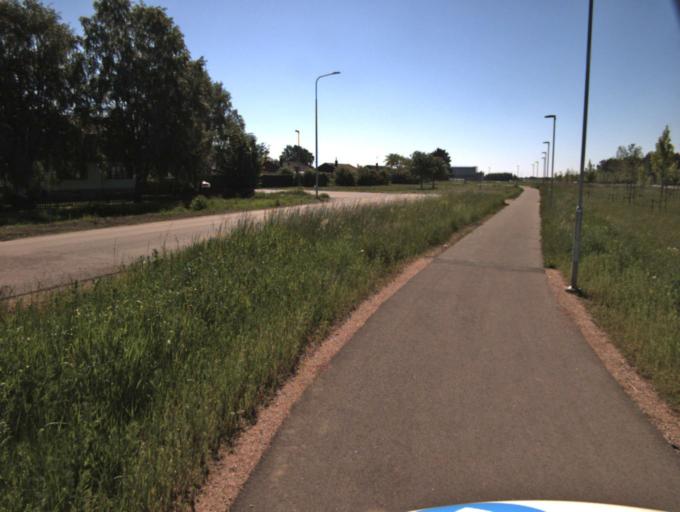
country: SE
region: Skane
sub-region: Kristianstads Kommun
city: Kristianstad
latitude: 56.0284
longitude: 14.1898
